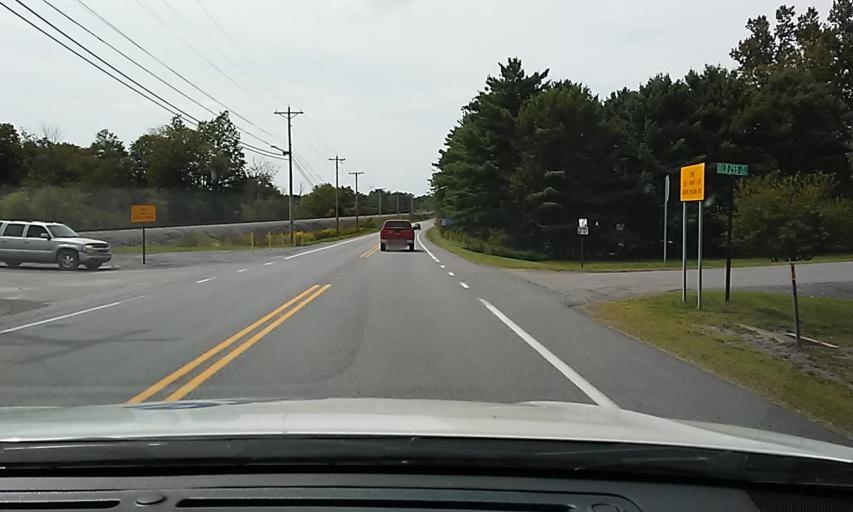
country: US
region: Pennsylvania
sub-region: Clearfield County
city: Treasure Lake
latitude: 41.1417
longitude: -78.6834
